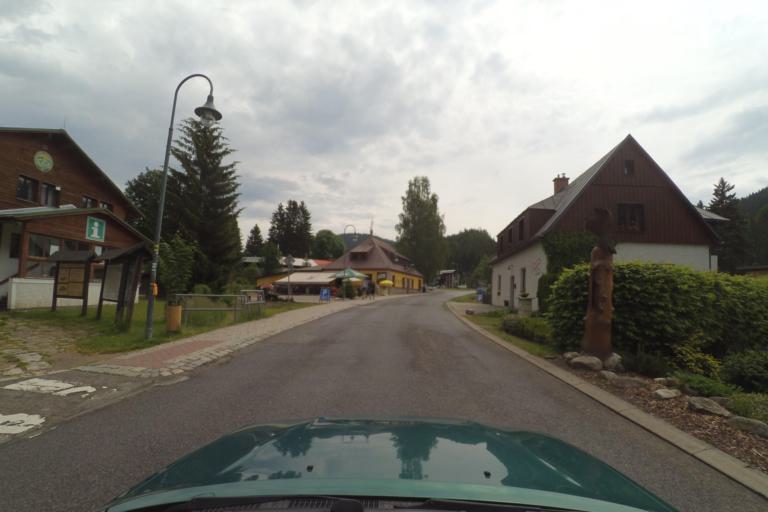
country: CZ
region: Liberecky
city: Harrachov
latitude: 50.7704
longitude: 15.4338
